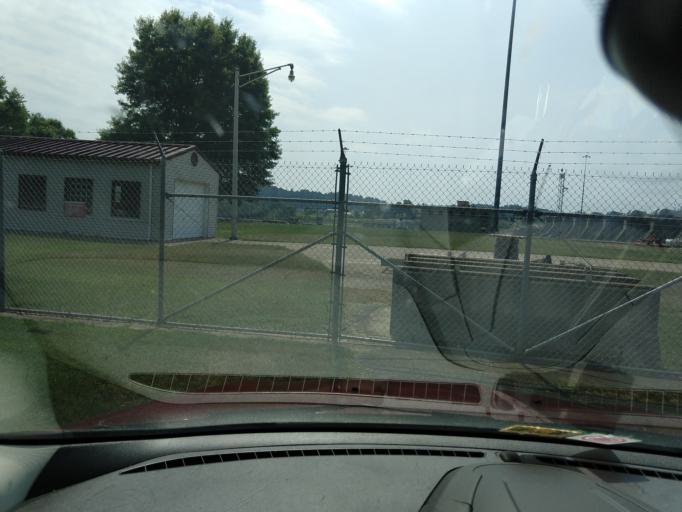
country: US
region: West Virginia
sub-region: Mason County
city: New Haven
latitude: 38.9196
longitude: -81.9128
